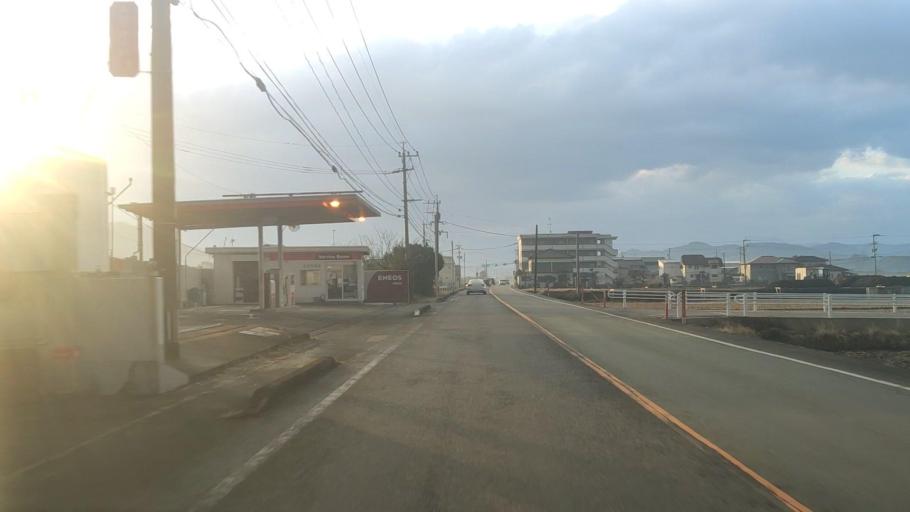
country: JP
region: Kumamoto
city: Uto
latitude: 32.7143
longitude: 130.7735
